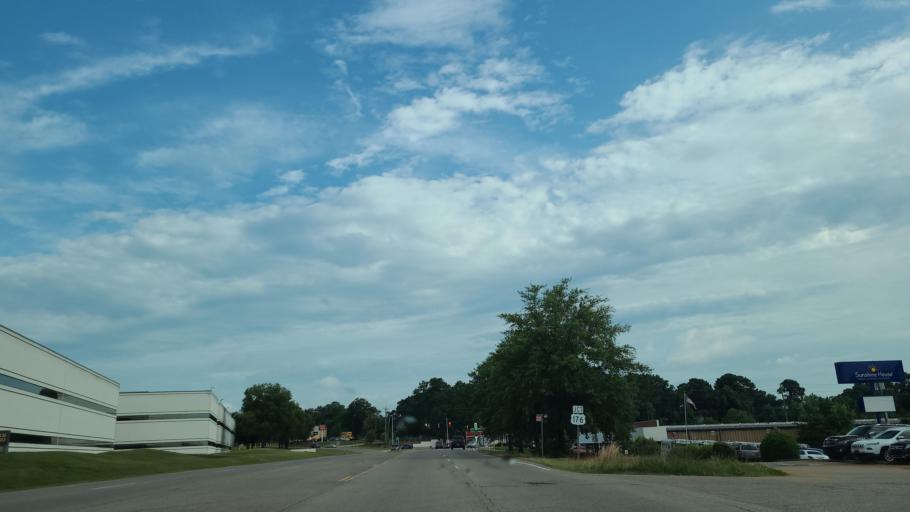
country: US
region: South Carolina
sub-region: Lexington County
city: West Columbia
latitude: 34.0232
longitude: -81.0781
